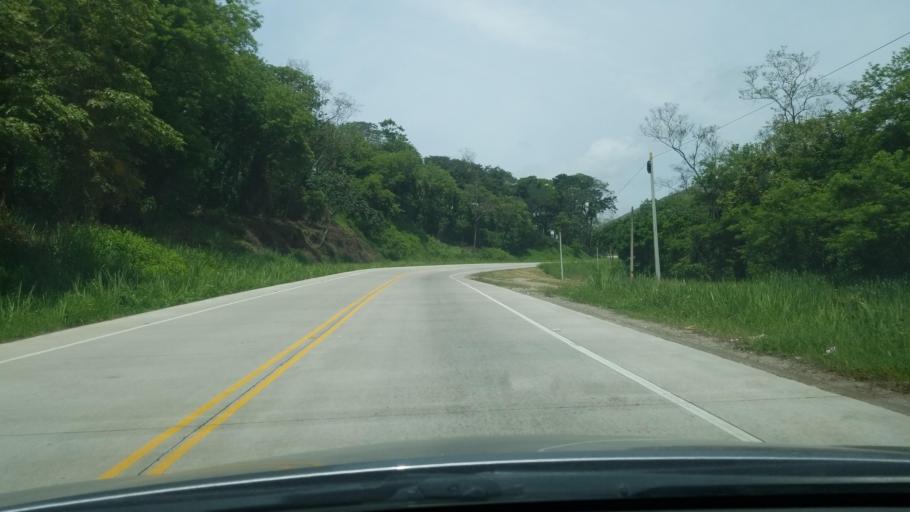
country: HN
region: Copan
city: Agua Caliente
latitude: 14.8721
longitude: -88.7816
